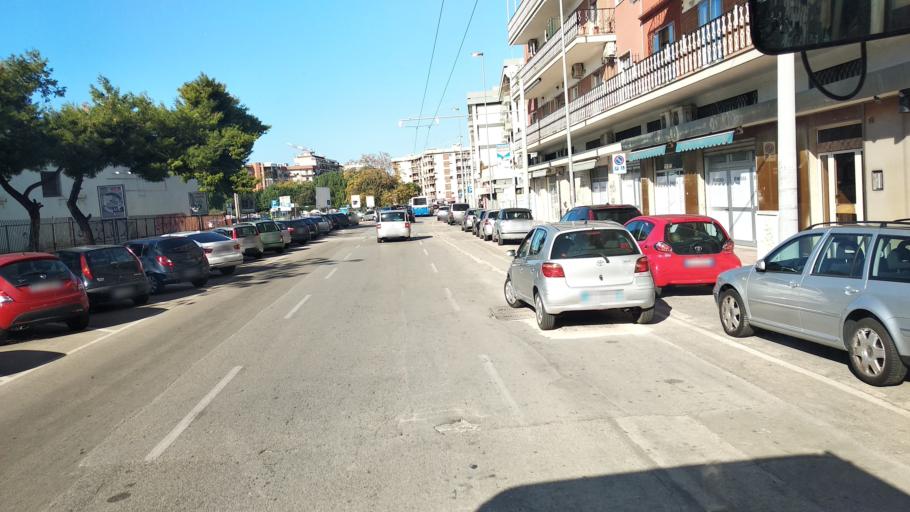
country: IT
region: Apulia
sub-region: Provincia di Bari
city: Bari
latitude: 41.1044
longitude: 16.8754
